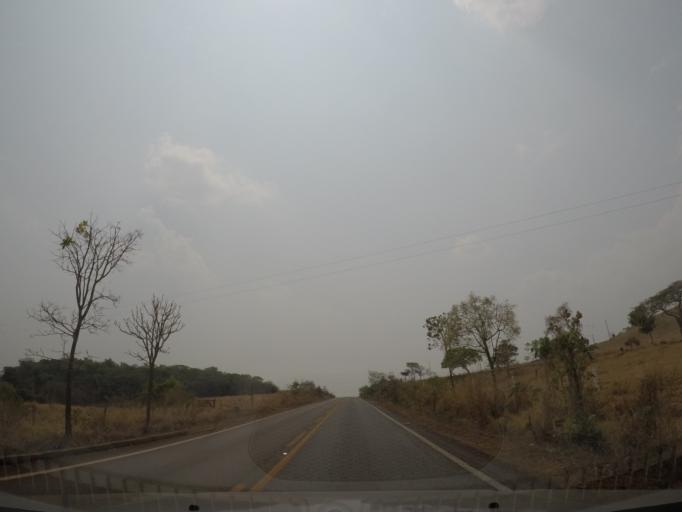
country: BR
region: Goias
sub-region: Pirenopolis
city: Pirenopolis
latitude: -15.9198
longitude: -48.8556
